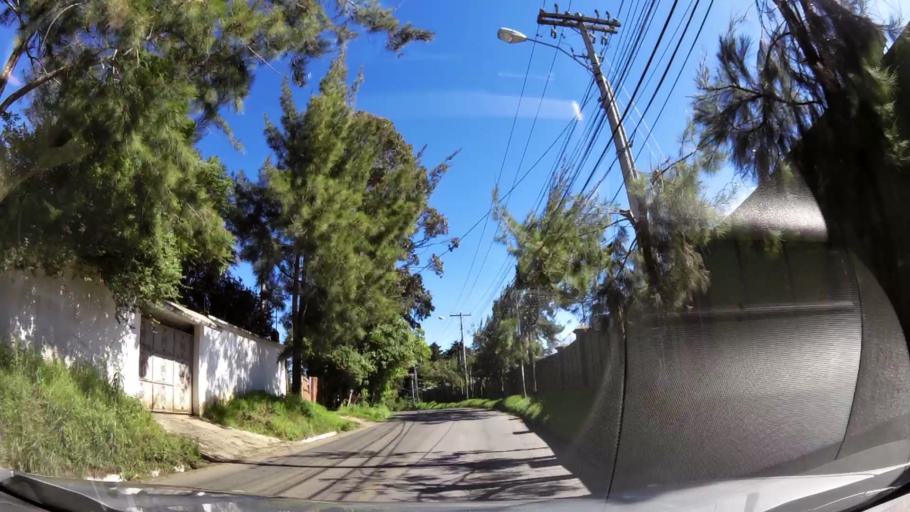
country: GT
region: Guatemala
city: San Jose Pinula
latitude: 14.5237
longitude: -90.4407
